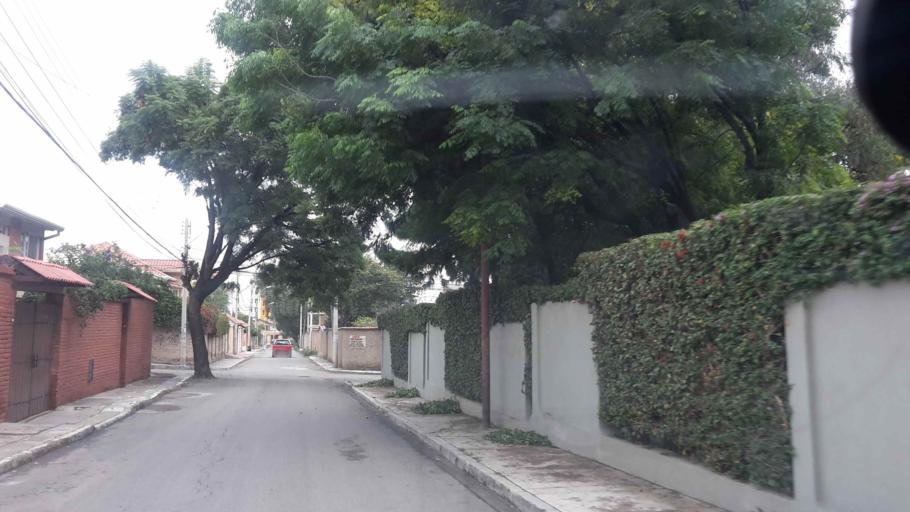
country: BO
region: Cochabamba
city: Cochabamba
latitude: -17.3625
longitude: -66.1773
